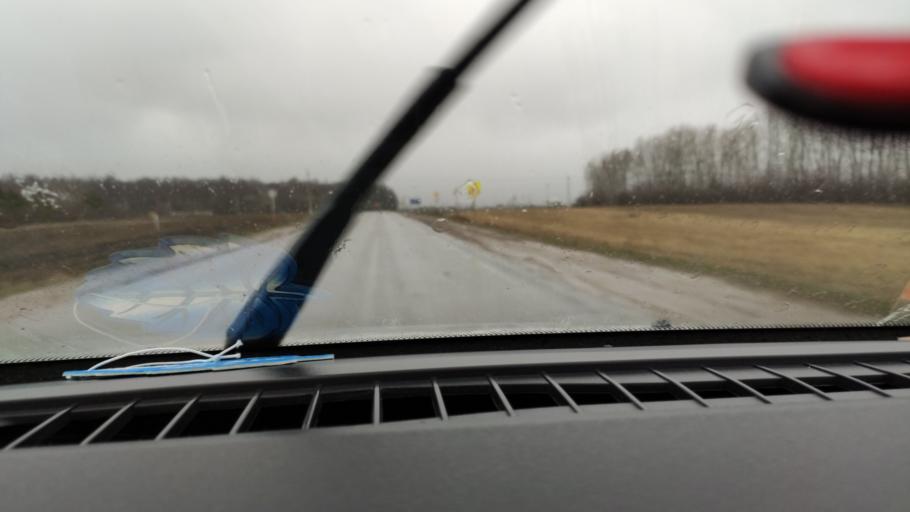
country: RU
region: Tatarstan
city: Cheremshan
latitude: 54.7322
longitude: 51.3322
